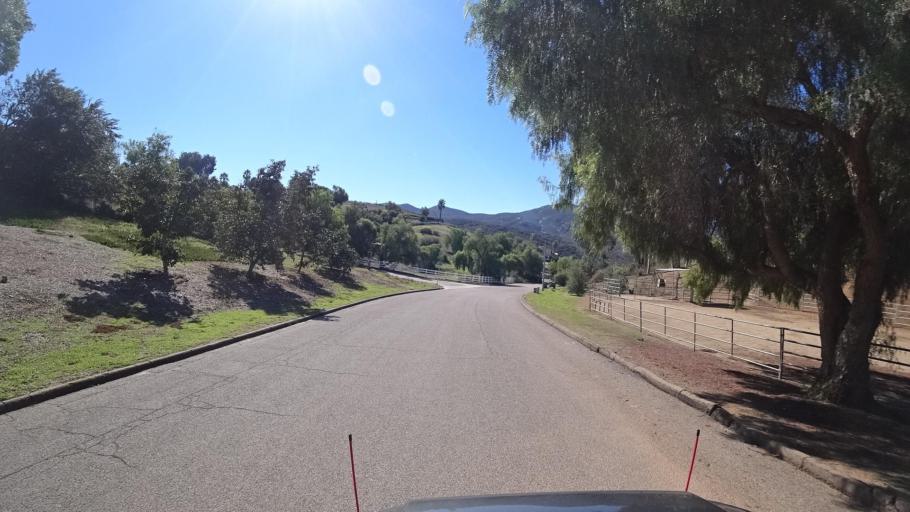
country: US
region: California
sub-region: San Diego County
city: Jamul
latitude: 32.7311
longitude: -116.9038
